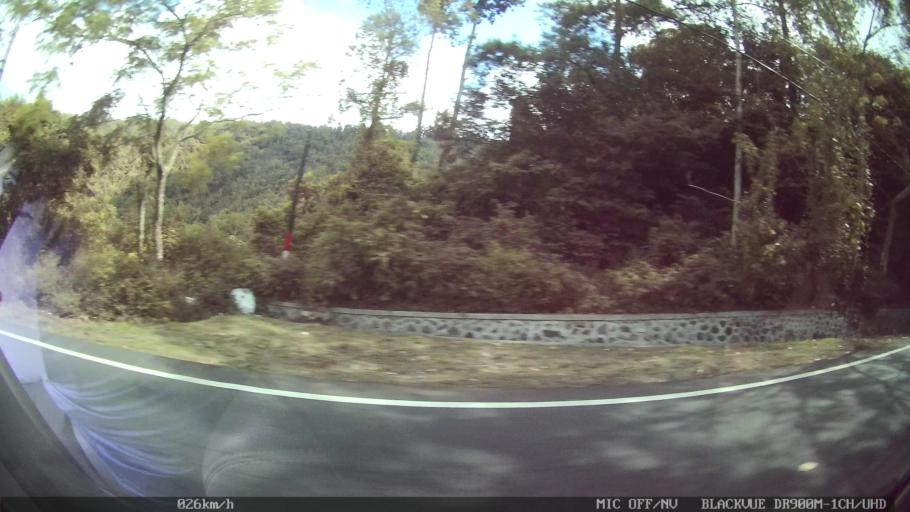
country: ID
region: Bali
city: Banjar Kedisan
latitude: -8.2801
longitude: 115.3688
